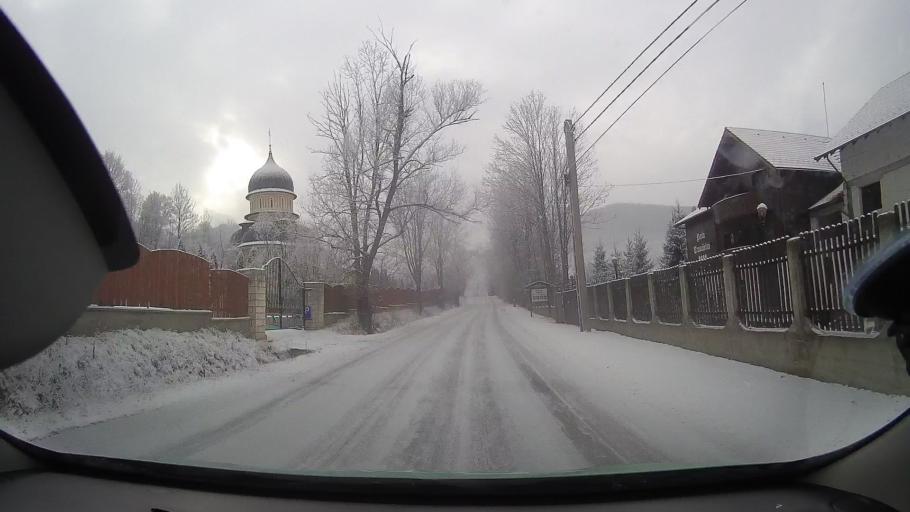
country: RO
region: Alba
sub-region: Comuna Rimetea
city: Rimetea
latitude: 46.4842
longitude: 23.5810
